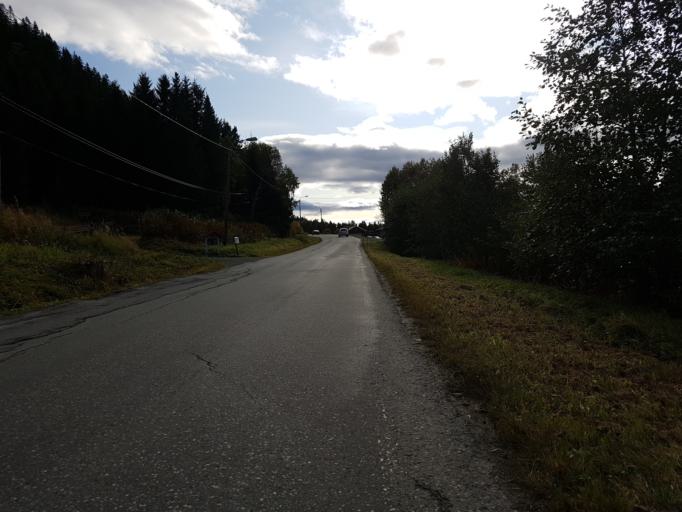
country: NO
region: Sor-Trondelag
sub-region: Klaebu
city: Klaebu
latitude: 63.3963
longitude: 10.5551
